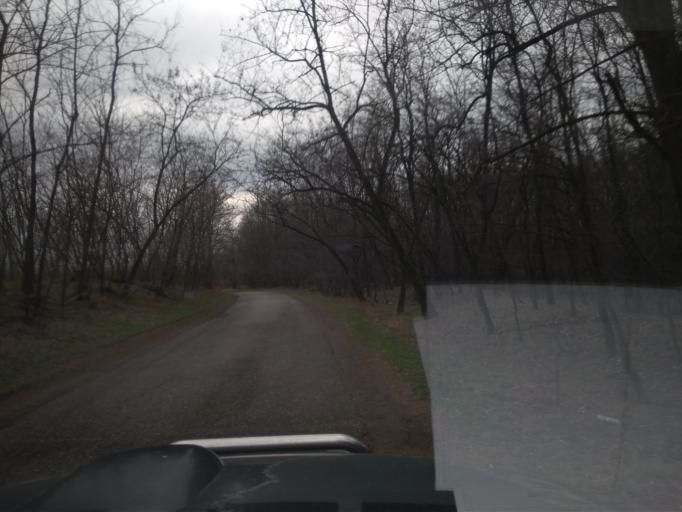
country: HU
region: Szabolcs-Szatmar-Bereg
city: Nyirpazony
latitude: 48.0178
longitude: 21.8081
